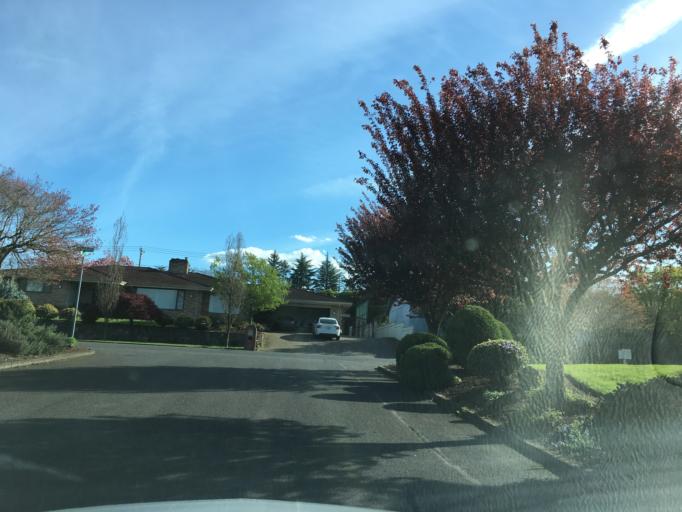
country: US
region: Oregon
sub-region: Multnomah County
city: Lents
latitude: 45.5465
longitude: -122.5307
